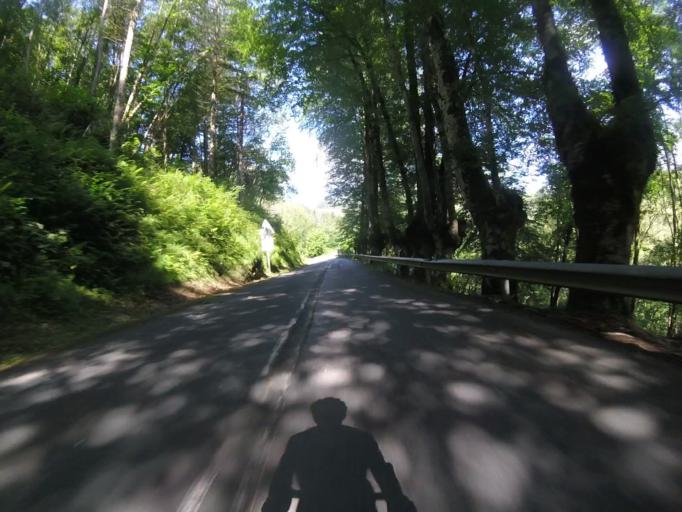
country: ES
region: Basque Country
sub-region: Provincia de Guipuzcoa
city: Beizama
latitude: 43.0972
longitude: -2.2405
